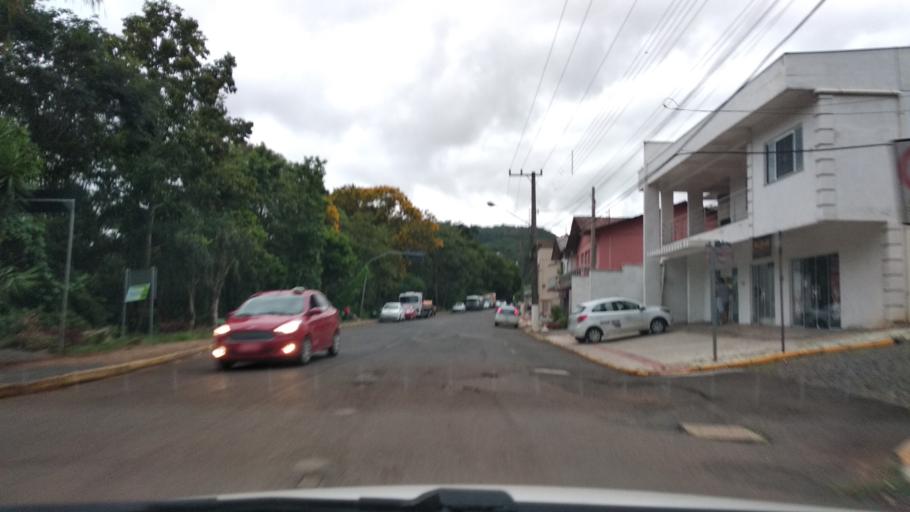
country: BR
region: Santa Catarina
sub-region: Videira
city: Videira
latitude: -27.0457
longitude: -51.2277
